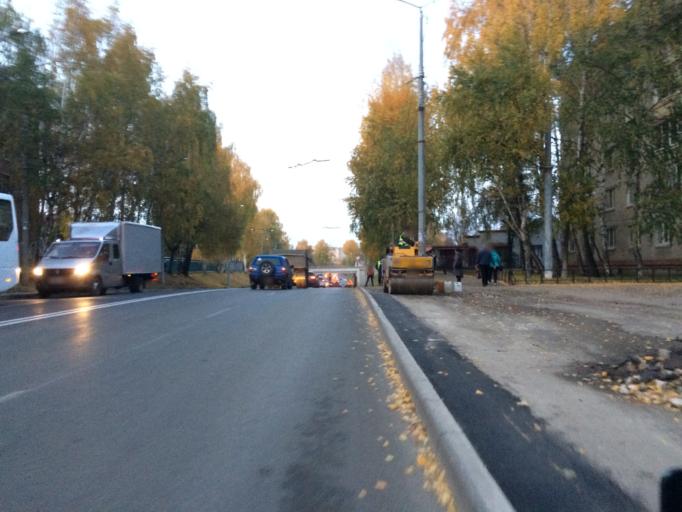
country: RU
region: Mariy-El
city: Yoshkar-Ola
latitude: 56.6169
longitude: 47.8843
